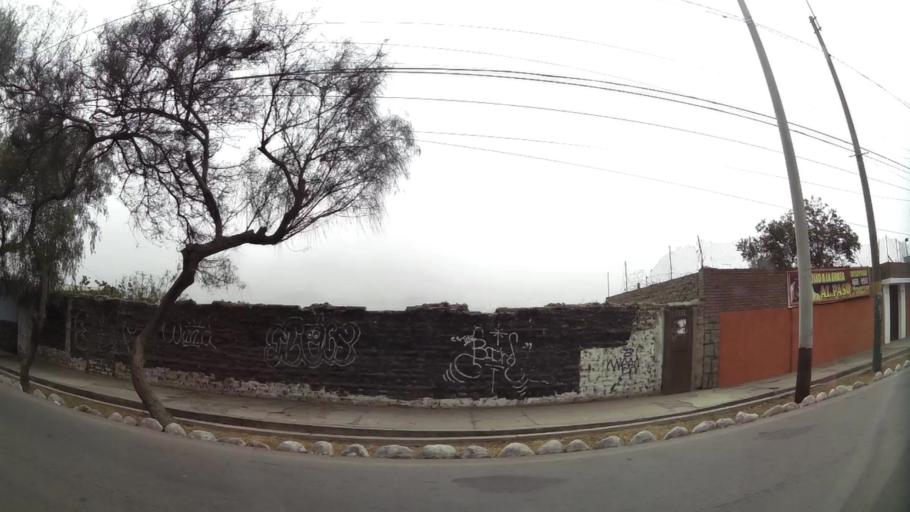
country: PE
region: Lima
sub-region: Lima
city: Chaclacayo
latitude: -11.9742
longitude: -76.7641
